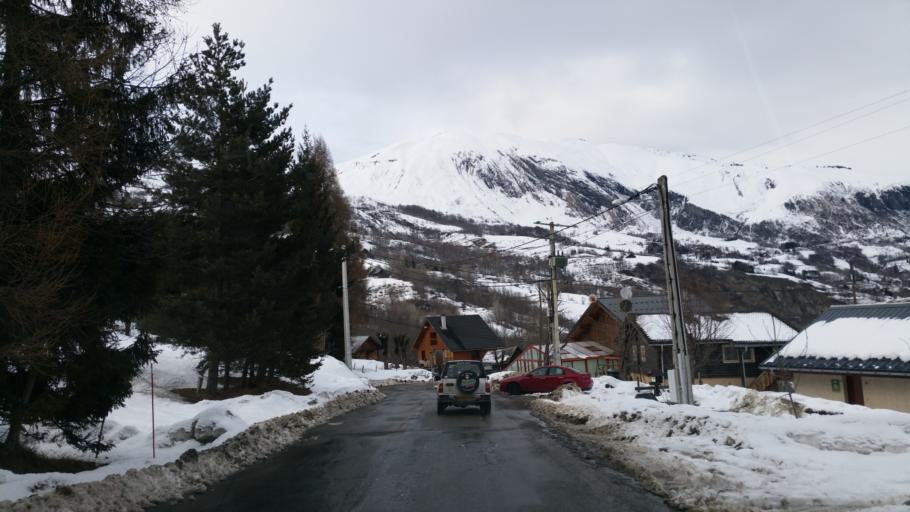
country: FR
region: Rhone-Alpes
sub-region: Departement de la Savoie
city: Saint-Jean-de-Maurienne
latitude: 45.2671
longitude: 6.3013
